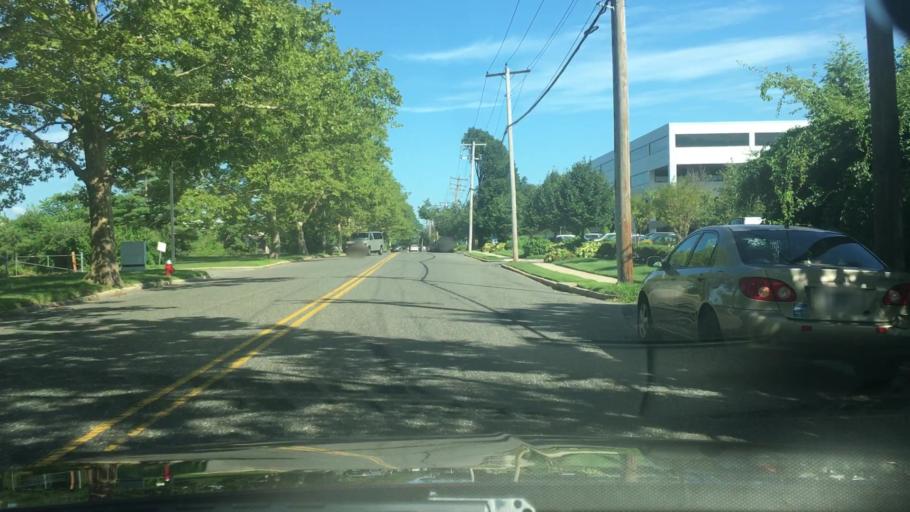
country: US
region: New York
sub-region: Suffolk County
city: Melville
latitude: 40.7736
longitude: -73.4260
